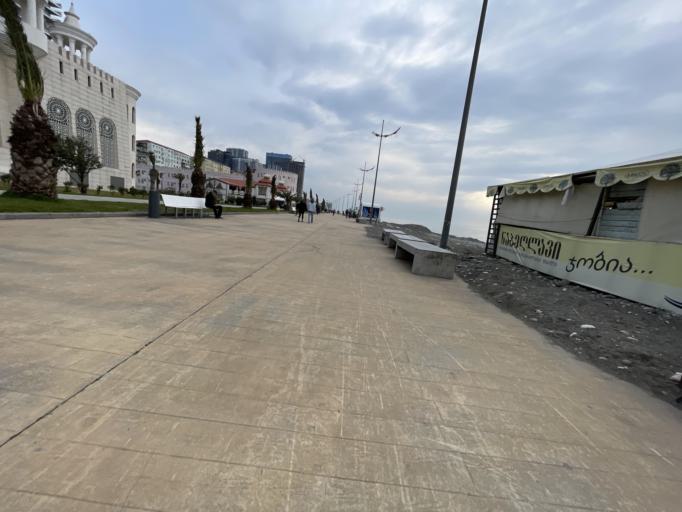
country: GE
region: Ajaria
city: Batumi
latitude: 41.6364
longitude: 41.6066
